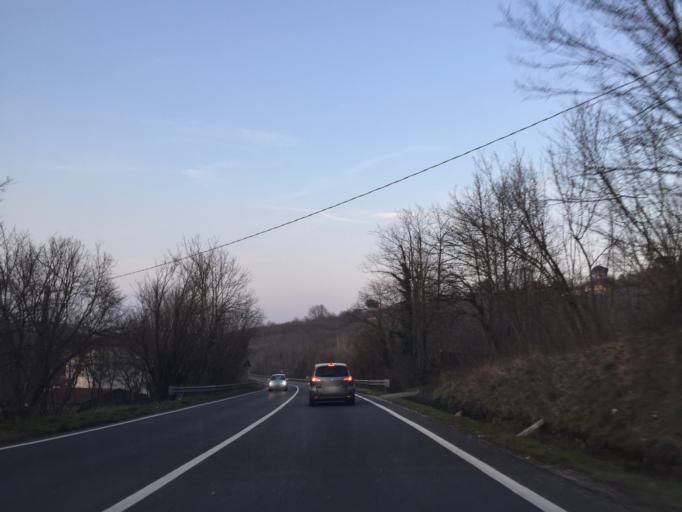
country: IT
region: Campania
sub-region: Provincia di Avellino
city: Avellino
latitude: 40.9044
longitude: 14.8081
